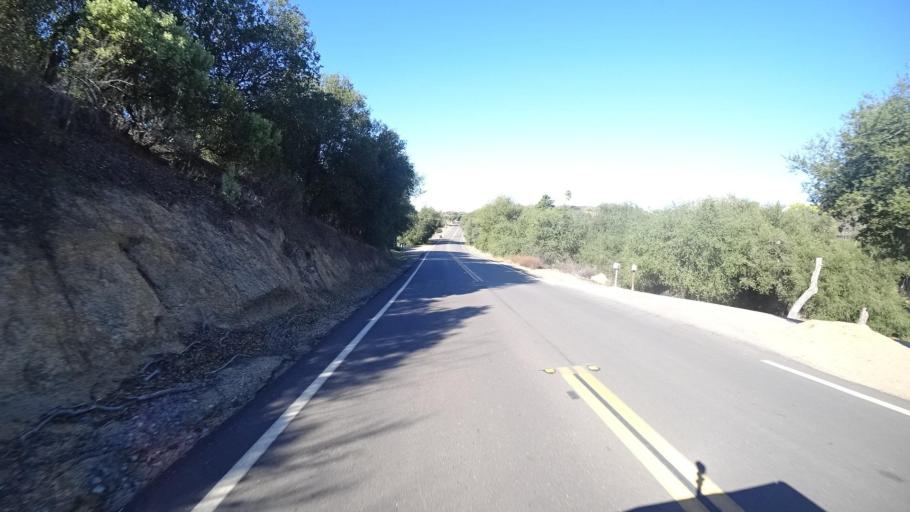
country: MX
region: Baja California
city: Tecate
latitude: 32.6763
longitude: -116.7231
